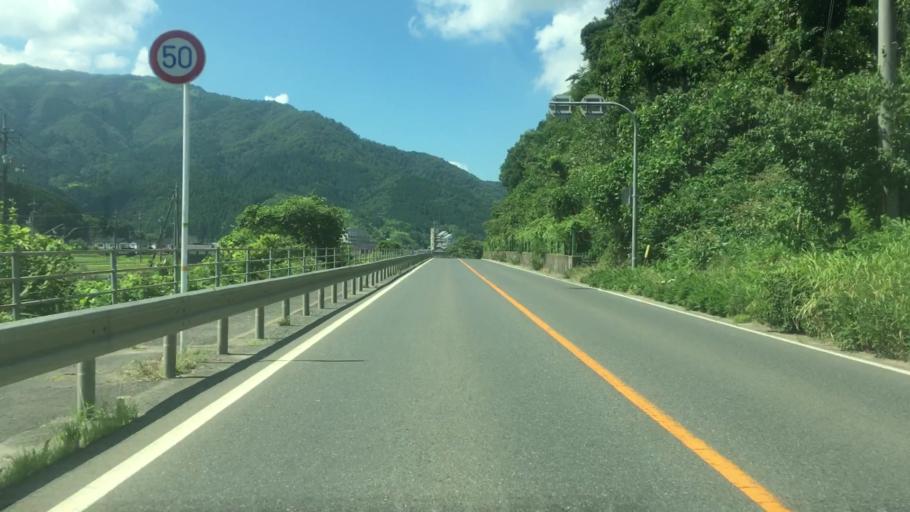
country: JP
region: Tottori
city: Tottori
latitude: 35.2563
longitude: 134.2289
